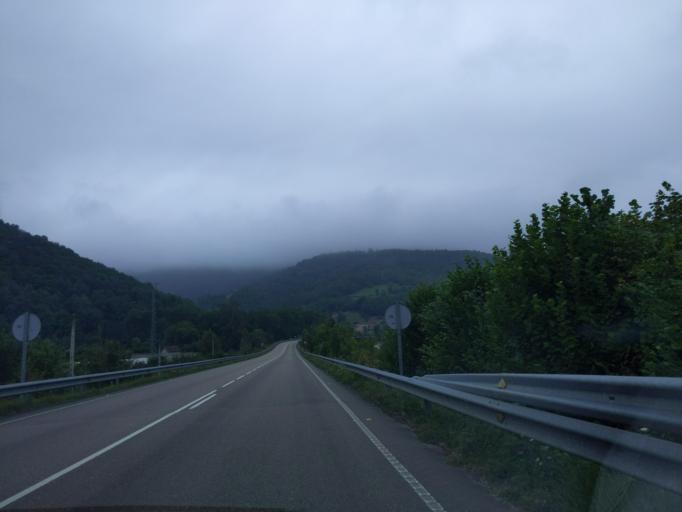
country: ES
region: Asturias
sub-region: Province of Asturias
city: Pola de Laviana
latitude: 43.2344
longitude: -5.5274
